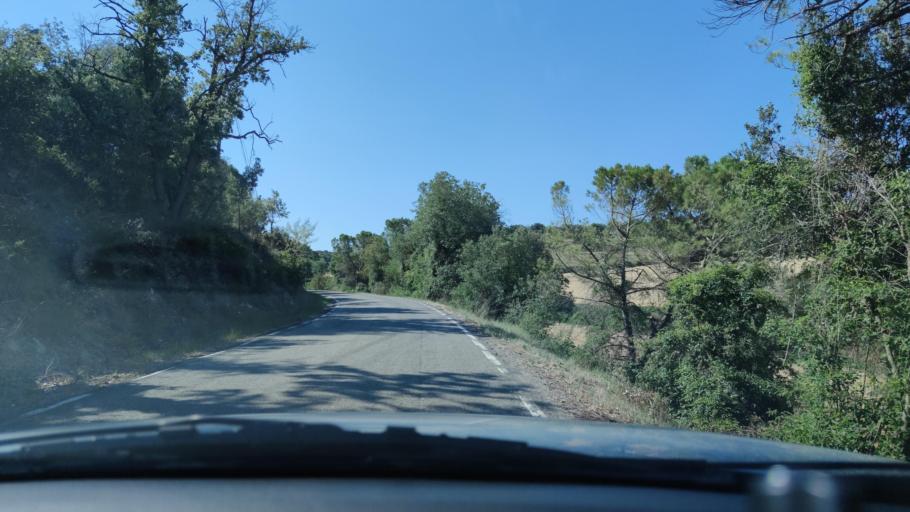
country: ES
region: Catalonia
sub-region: Provincia de Lleida
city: Sant Guim de Freixenet
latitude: 41.6766
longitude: 1.4041
